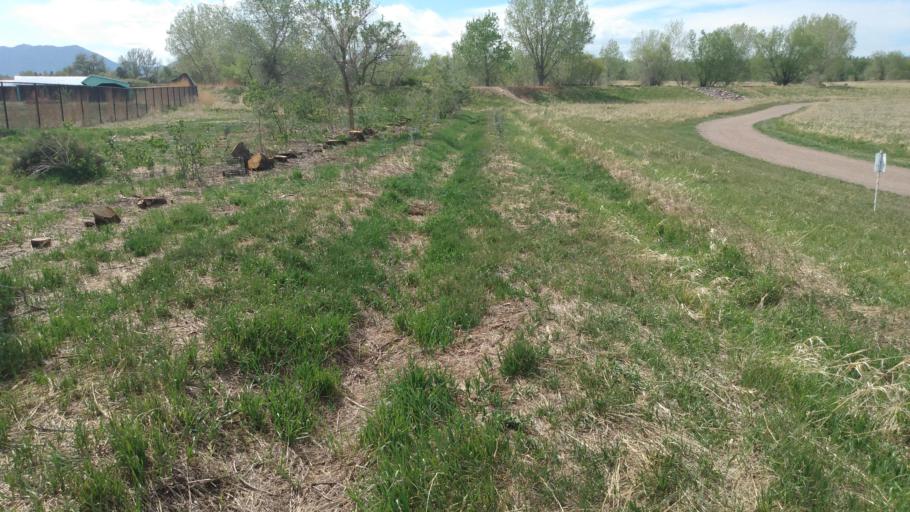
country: US
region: Colorado
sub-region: Boulder County
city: Louisville
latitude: 39.9690
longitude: -105.1424
